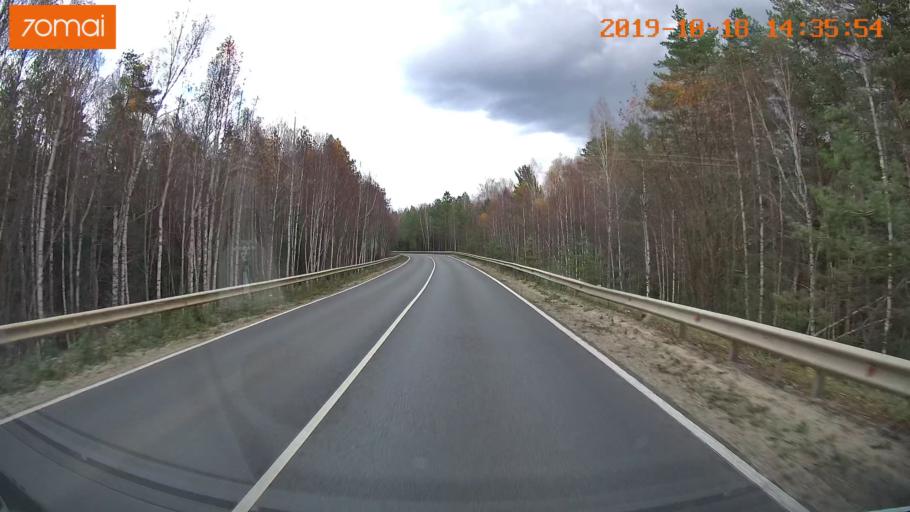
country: RU
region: Vladimir
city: Velikodvorskiy
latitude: 55.2214
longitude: 40.6492
